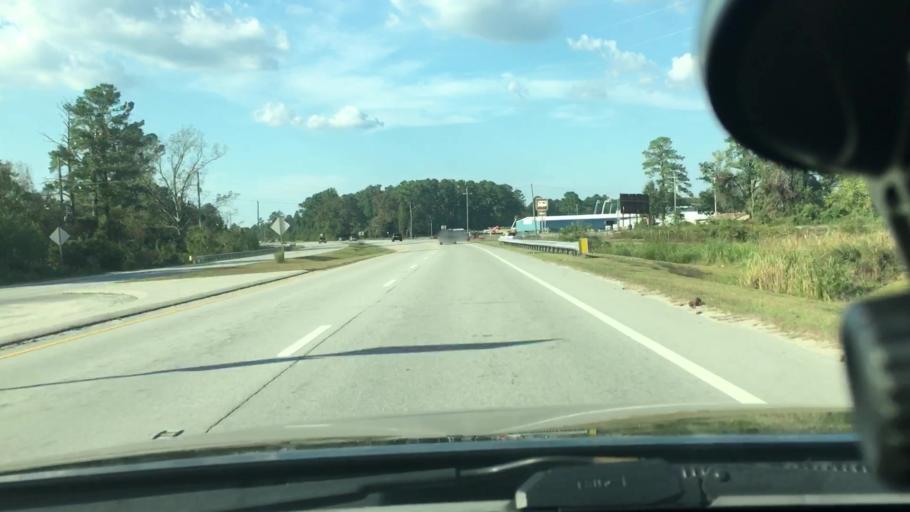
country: US
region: North Carolina
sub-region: Craven County
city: New Bern
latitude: 35.1331
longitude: -77.0264
